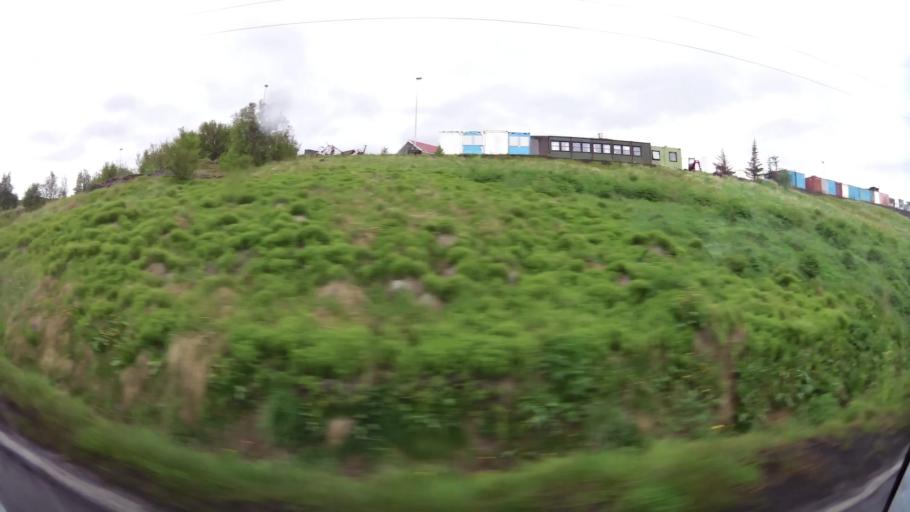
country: IS
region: Northeast
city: Akureyri
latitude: 65.7020
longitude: -18.1176
